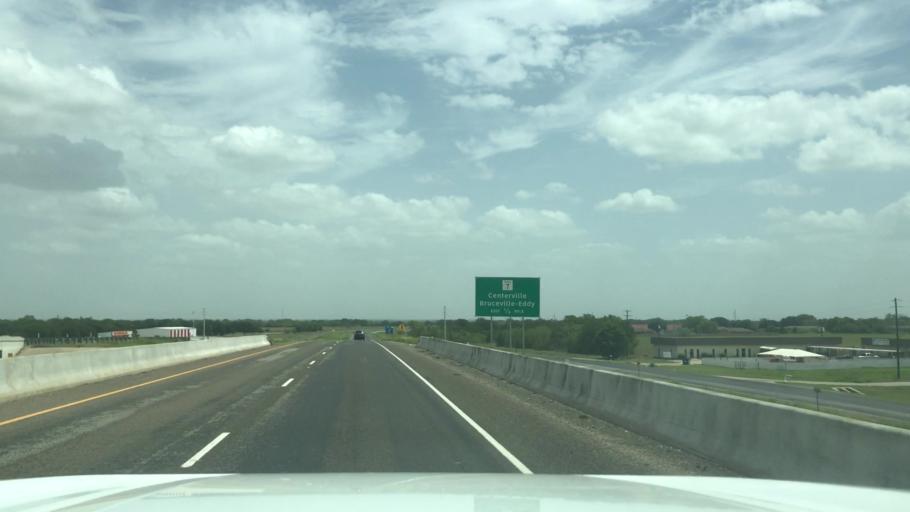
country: US
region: Texas
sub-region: Falls County
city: Marlin
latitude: 31.3208
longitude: -96.8828
